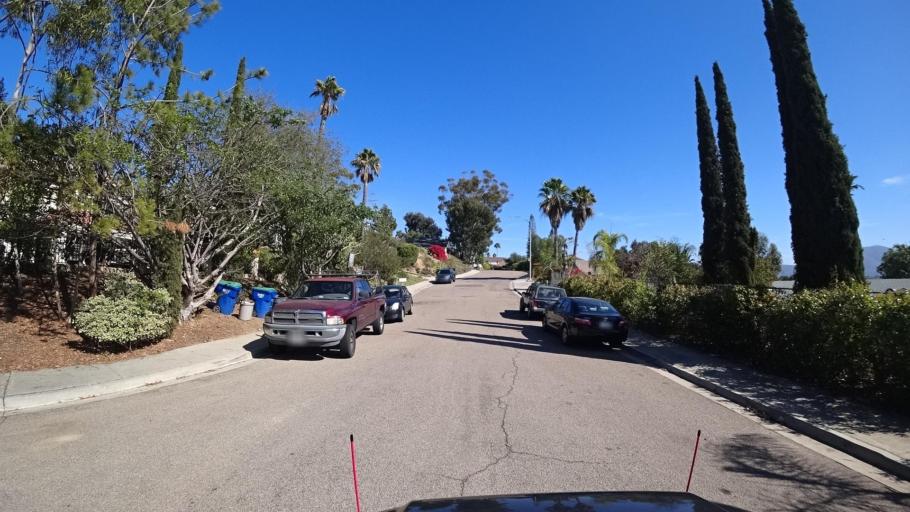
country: US
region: California
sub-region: San Diego County
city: Casa de Oro-Mount Helix
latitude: 32.7567
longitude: -116.9849
